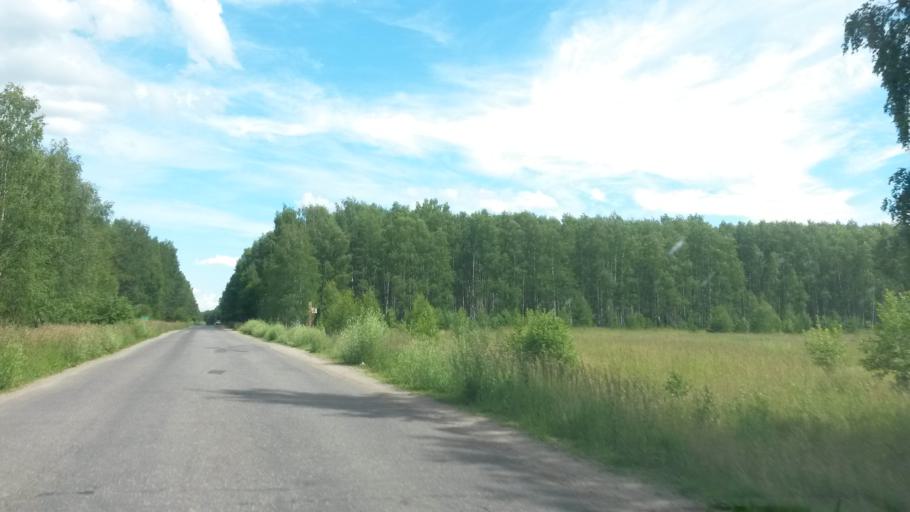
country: RU
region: Ivanovo
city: Zavolzhsk
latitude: 57.4653
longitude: 42.1830
